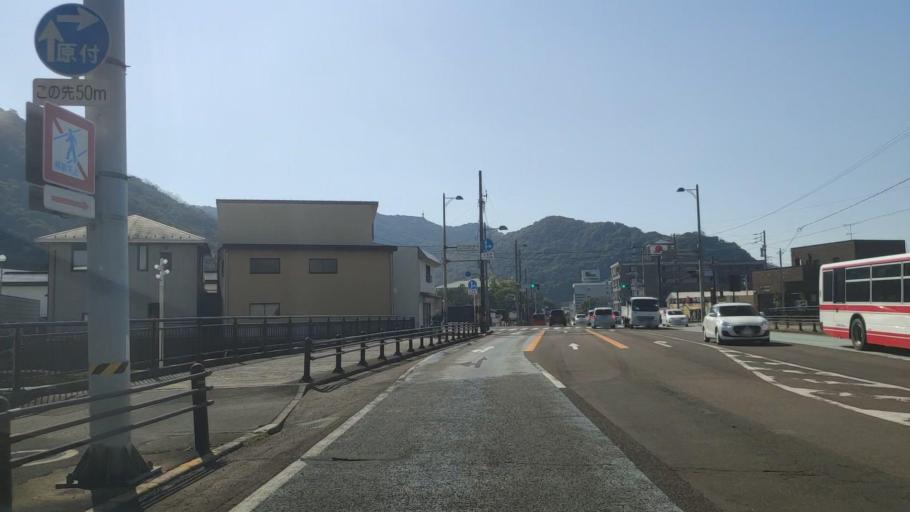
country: JP
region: Gifu
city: Gifu-shi
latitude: 35.4365
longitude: 136.7733
